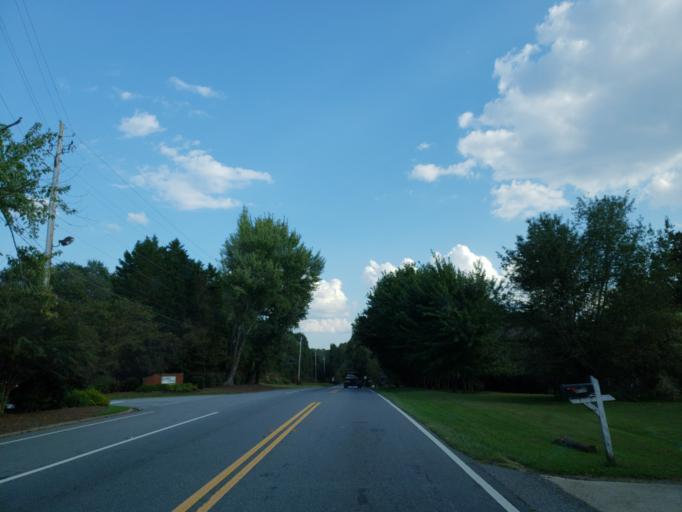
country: US
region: Georgia
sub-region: Fulton County
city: Roswell
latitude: 34.0660
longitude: -84.3491
